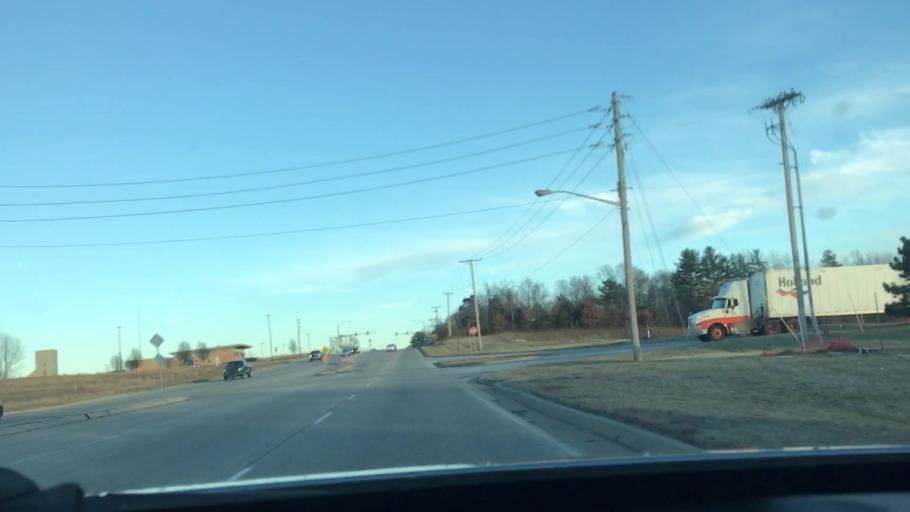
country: US
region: Kansas
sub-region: Wyandotte County
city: Edwardsville
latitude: 39.1163
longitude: -94.8056
